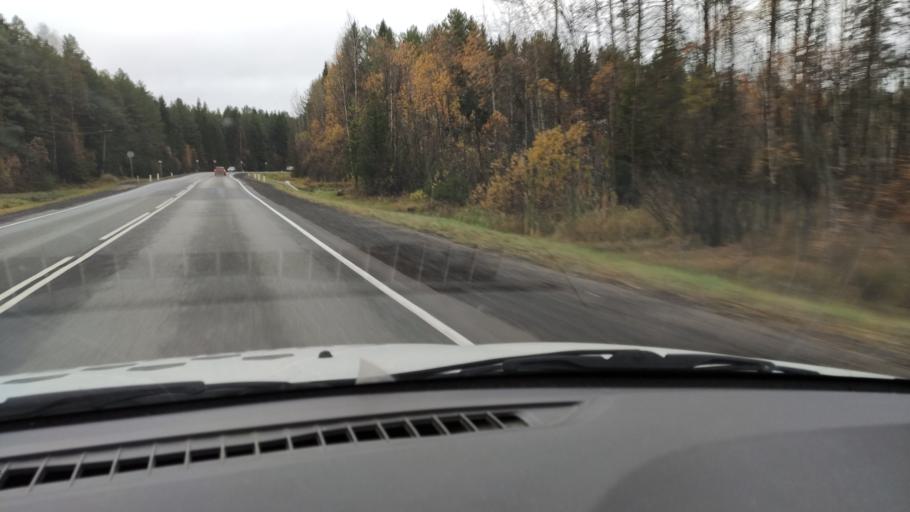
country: RU
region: Kirov
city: Belaya Kholunitsa
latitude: 58.8797
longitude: 50.8710
